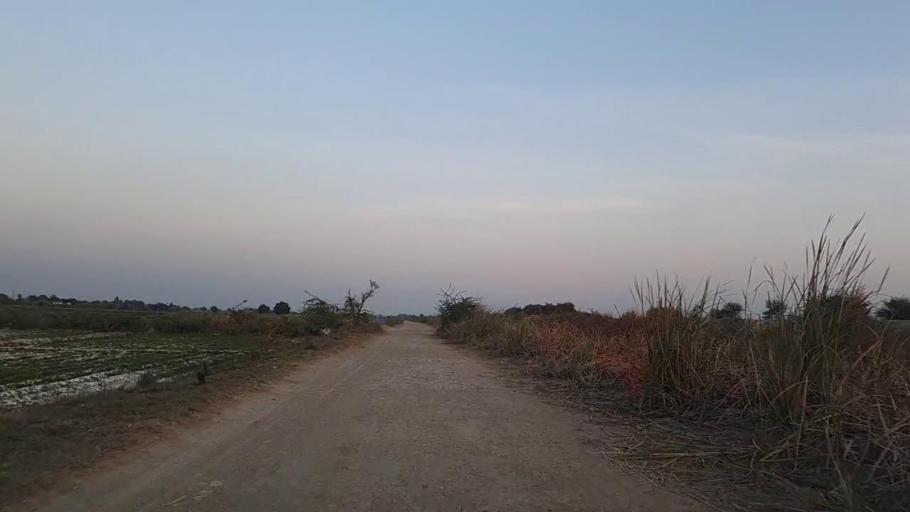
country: PK
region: Sindh
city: Tando Mittha Khan
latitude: 25.9419
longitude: 69.1377
